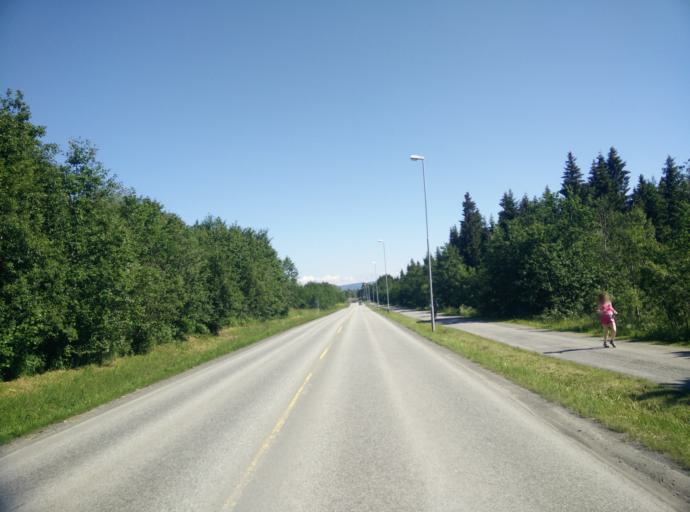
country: NO
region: Sor-Trondelag
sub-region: Trondheim
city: Trondheim
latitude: 63.3733
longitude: 10.3307
